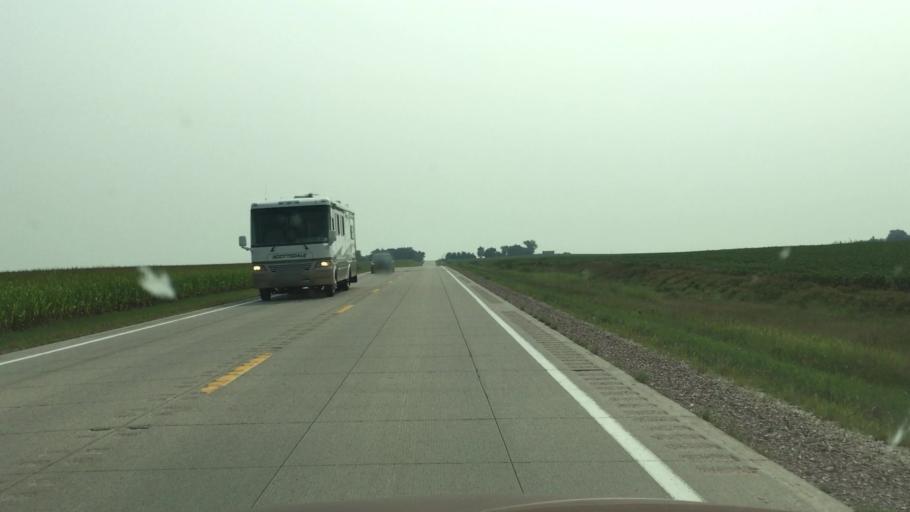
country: US
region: Iowa
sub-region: Osceola County
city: Sibley
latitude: 43.4328
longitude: -95.6754
